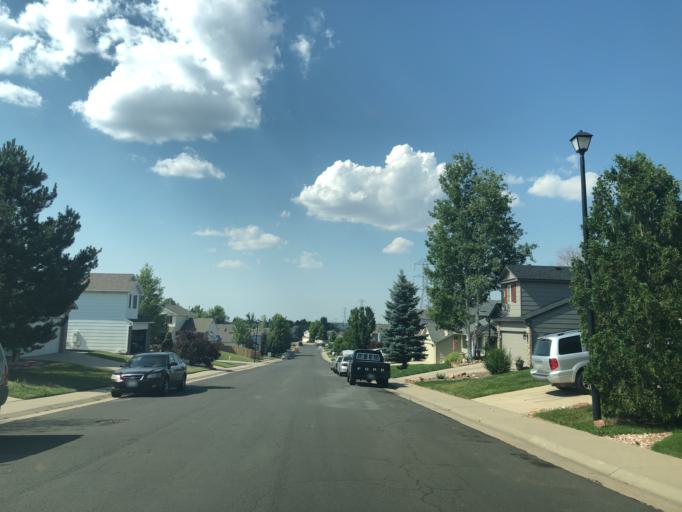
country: US
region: Colorado
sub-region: Arapahoe County
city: Dove Valley
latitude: 39.6345
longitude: -104.7549
